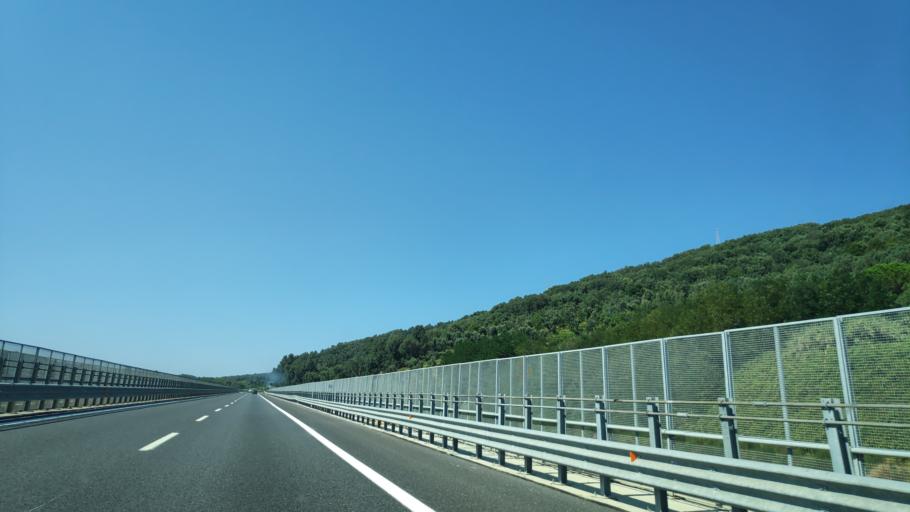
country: IT
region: Calabria
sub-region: Provincia di Reggio Calabria
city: Seminara
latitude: 38.3390
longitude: 15.8643
